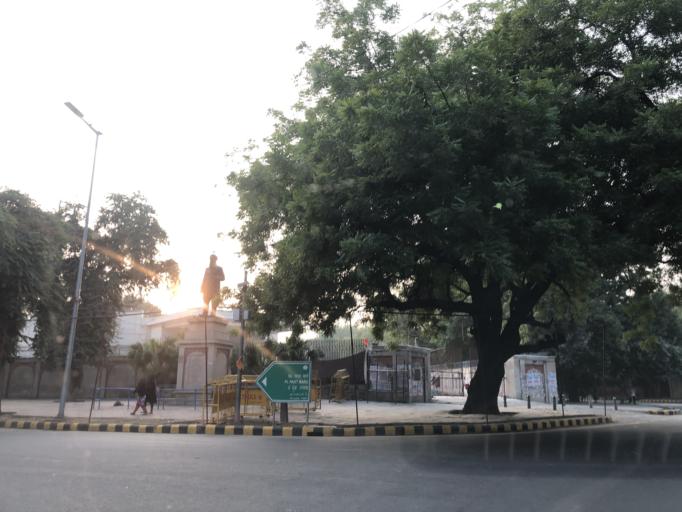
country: IN
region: NCT
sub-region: New Delhi
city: New Delhi
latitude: 28.6201
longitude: 77.2063
